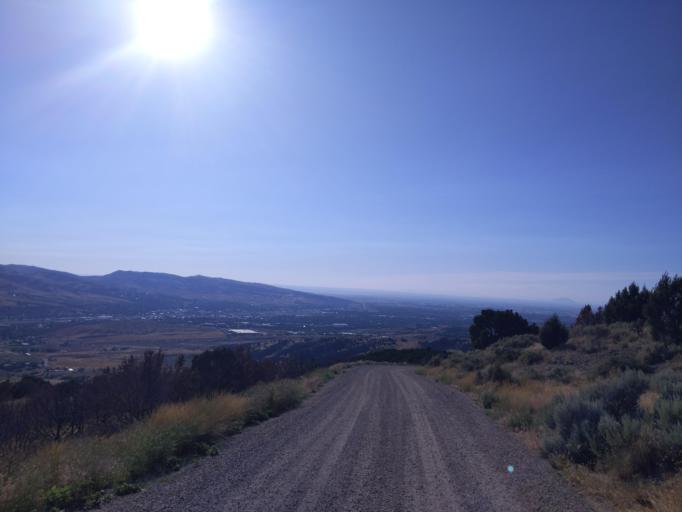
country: US
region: Idaho
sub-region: Bannock County
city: Pocatello
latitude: 42.8517
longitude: -112.3799
